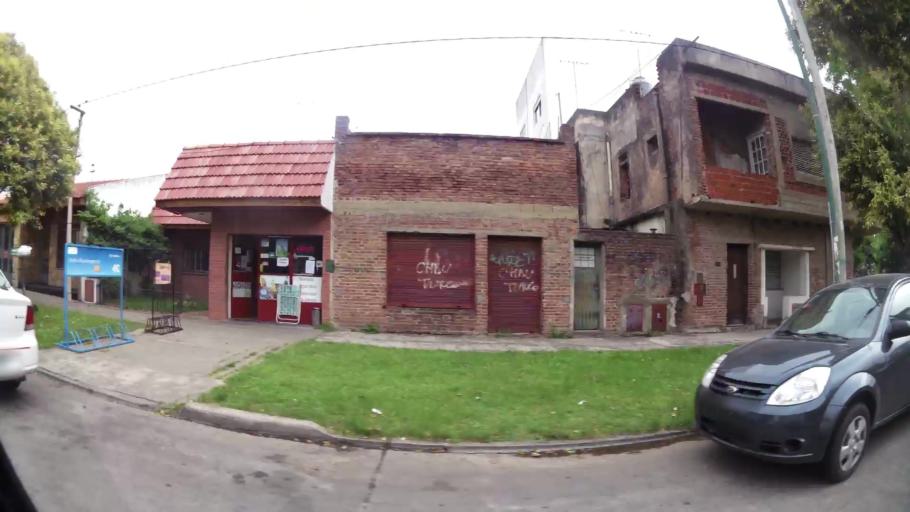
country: AR
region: Buenos Aires
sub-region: Partido de La Plata
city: La Plata
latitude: -34.9261
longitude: -57.9759
